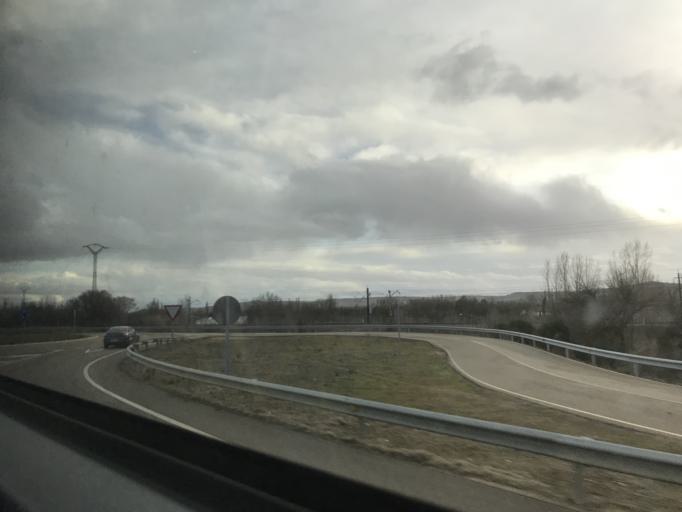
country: ES
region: Castille and Leon
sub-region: Provincia de Palencia
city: Grijota
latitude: 42.0314
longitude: -4.5550
